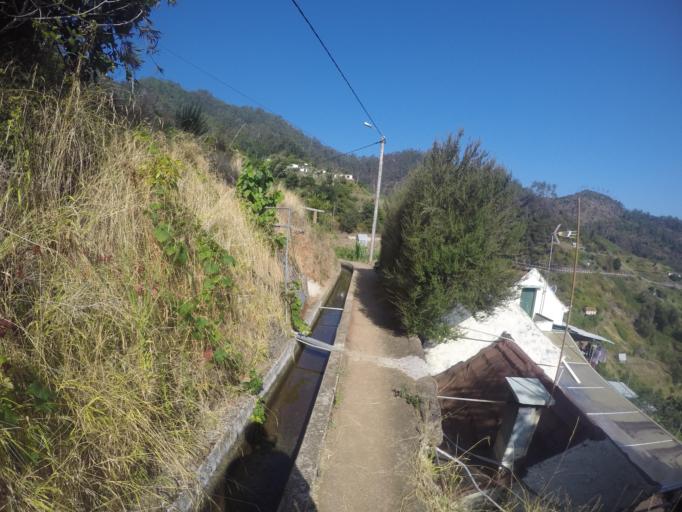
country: PT
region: Madeira
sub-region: Santana
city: Santana
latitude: 32.7643
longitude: -16.8229
